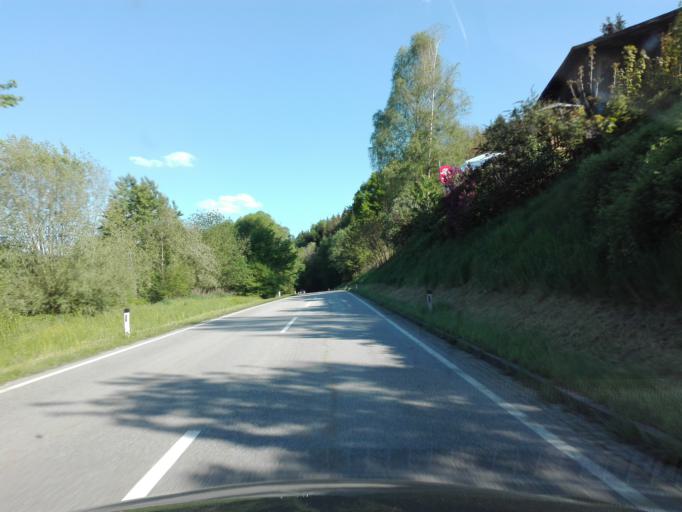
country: AT
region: Upper Austria
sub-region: Politischer Bezirk Rohrbach
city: Pfarrkirchen im Muehlkreis
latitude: 48.4826
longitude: 13.7551
